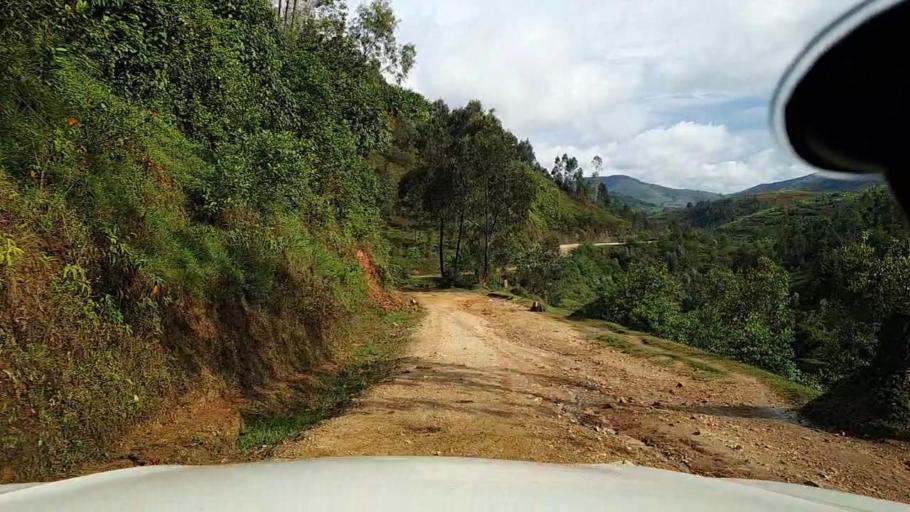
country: RW
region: Western Province
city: Kibuye
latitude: -2.1236
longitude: 29.4967
